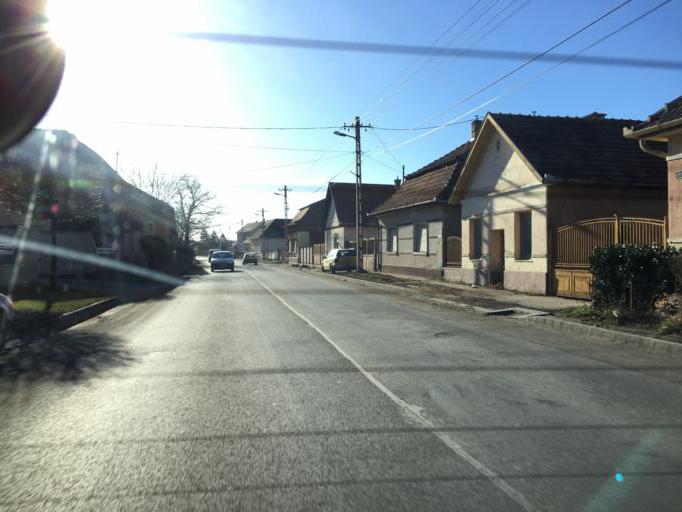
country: HU
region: Pest
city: Kiskunlachaza
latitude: 47.1744
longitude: 18.9991
